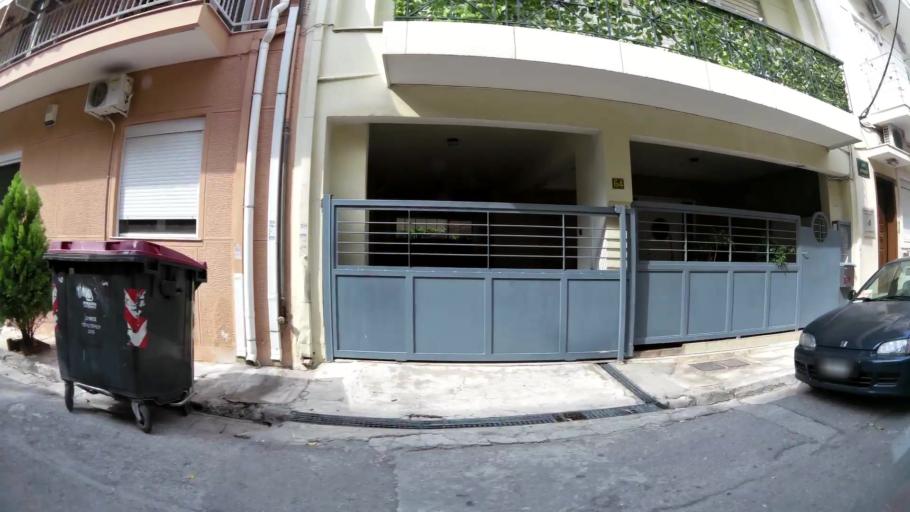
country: GR
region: Attica
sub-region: Nomarchia Athinas
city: Peristeri
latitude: 38.0091
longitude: 23.6828
